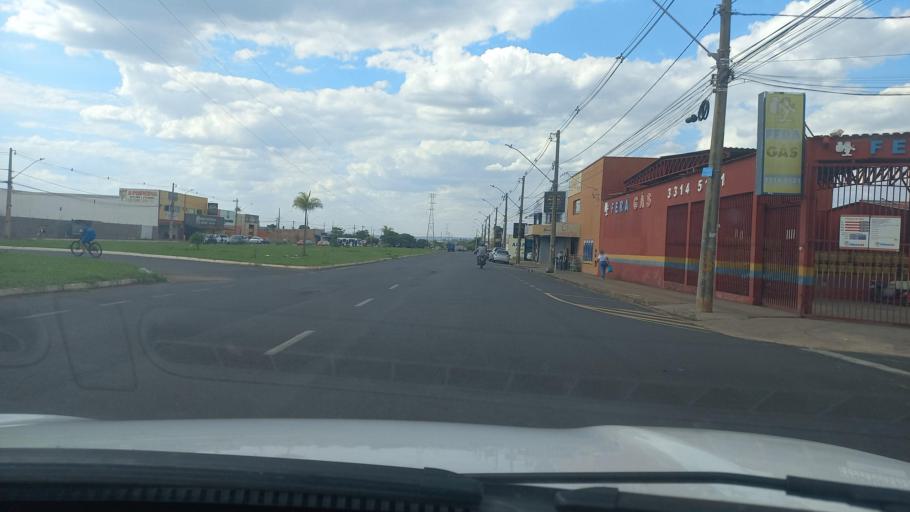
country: BR
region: Minas Gerais
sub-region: Uberaba
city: Uberaba
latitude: -19.7575
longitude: -47.9890
